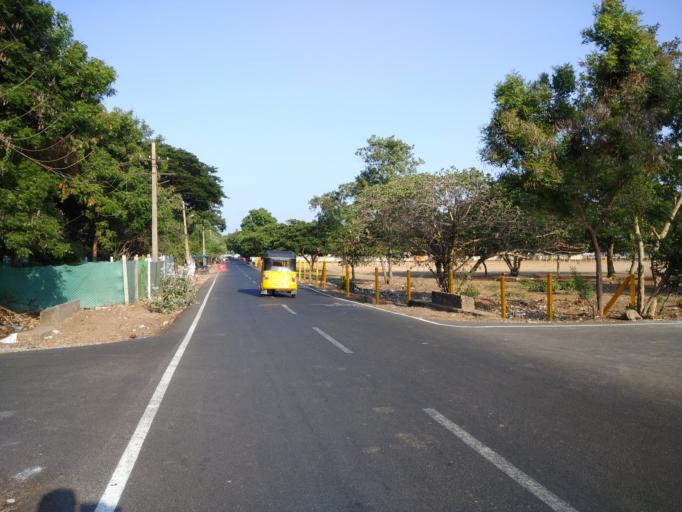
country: IN
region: Tamil Nadu
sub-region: Kancheepuram
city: Saint Thomas Mount
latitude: 13.0157
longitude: 80.1867
